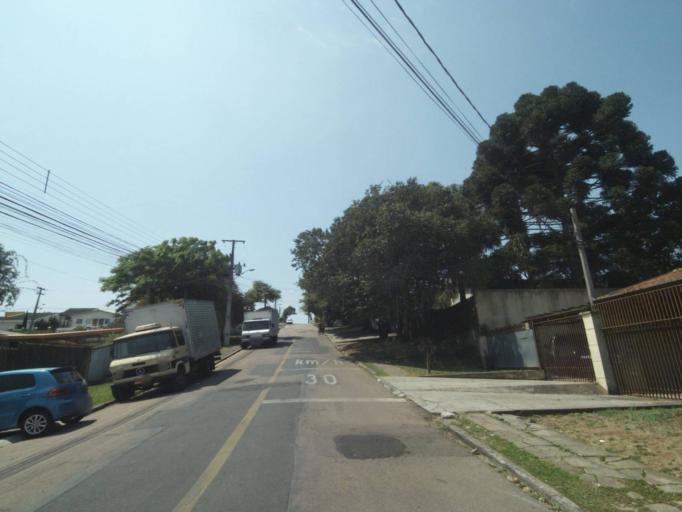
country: BR
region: Parana
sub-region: Curitiba
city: Curitiba
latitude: -25.4783
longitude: -49.3170
